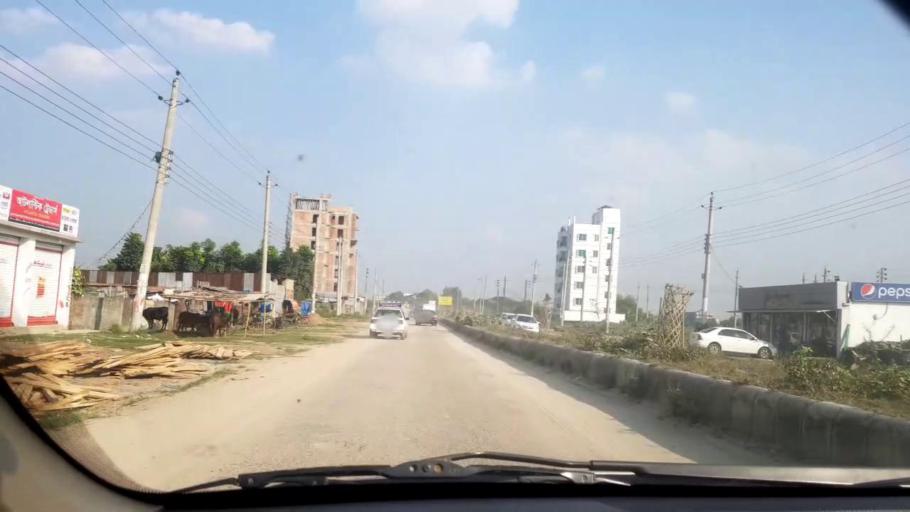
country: BD
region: Dhaka
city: Tungi
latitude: 23.8674
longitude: 90.3719
